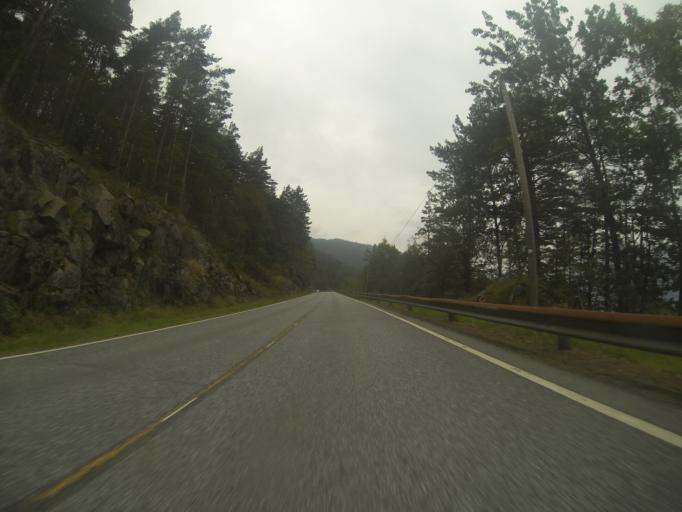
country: NO
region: Rogaland
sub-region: Suldal
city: Sand
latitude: 59.5230
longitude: 6.2463
